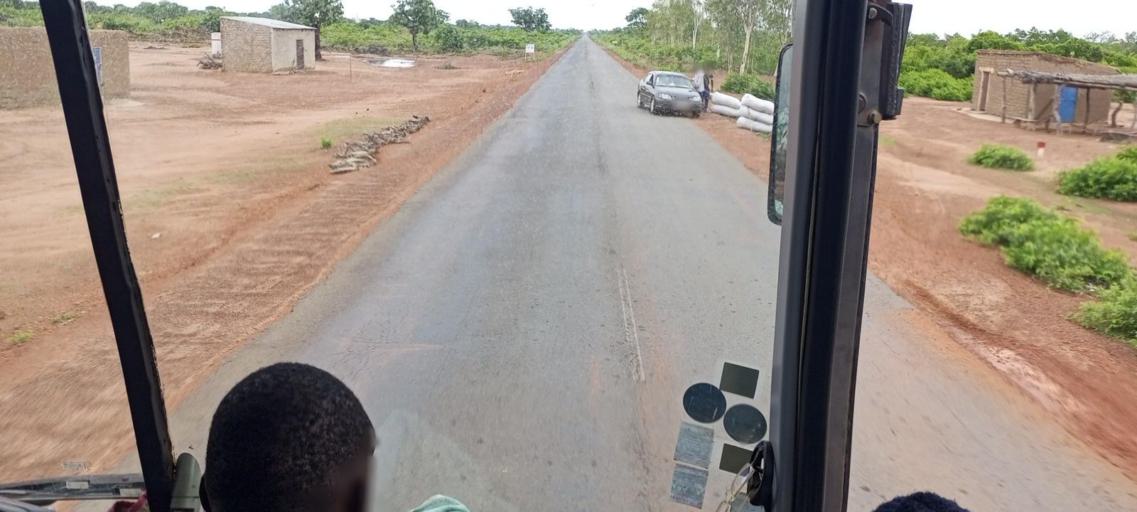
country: ML
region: Sikasso
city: Koutiala
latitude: 12.5564
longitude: -5.5893
